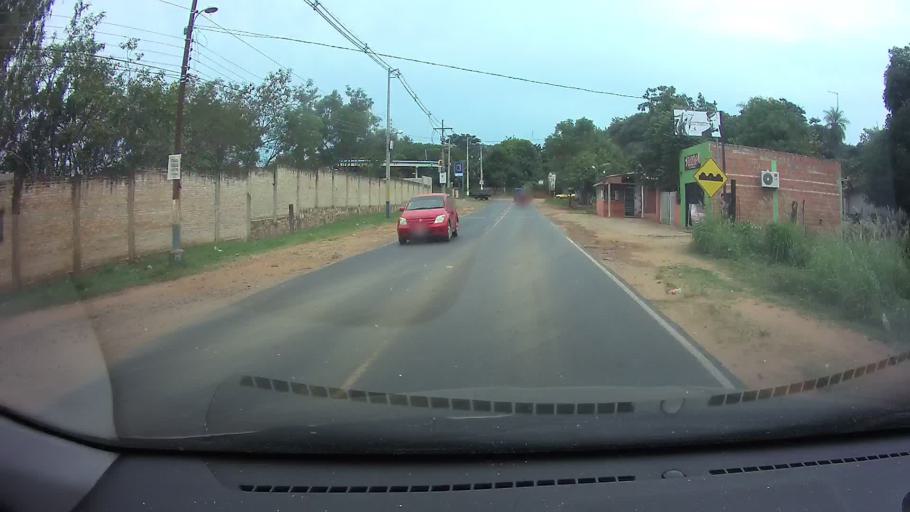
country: PY
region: Central
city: Limpio
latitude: -25.2214
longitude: -57.4774
